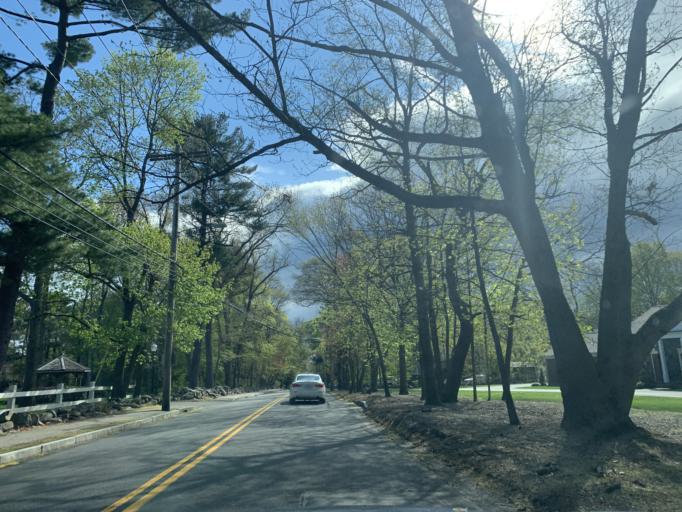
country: US
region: Massachusetts
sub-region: Norfolk County
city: Milton
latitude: 42.2578
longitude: -71.0636
